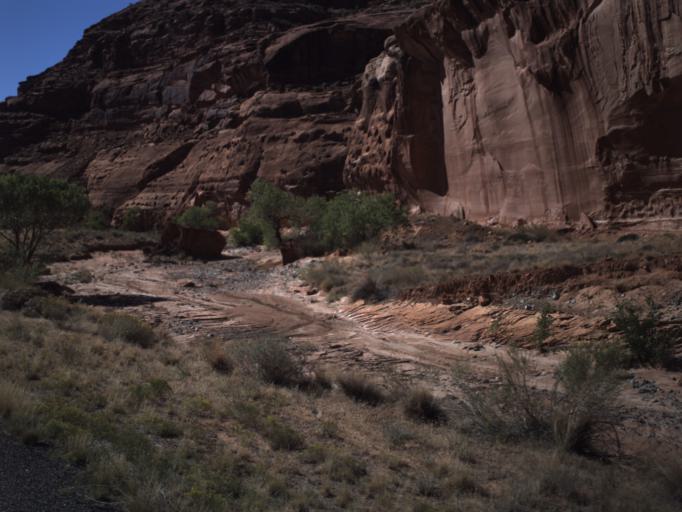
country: US
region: Utah
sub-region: San Juan County
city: Blanding
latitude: 37.9870
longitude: -110.4932
